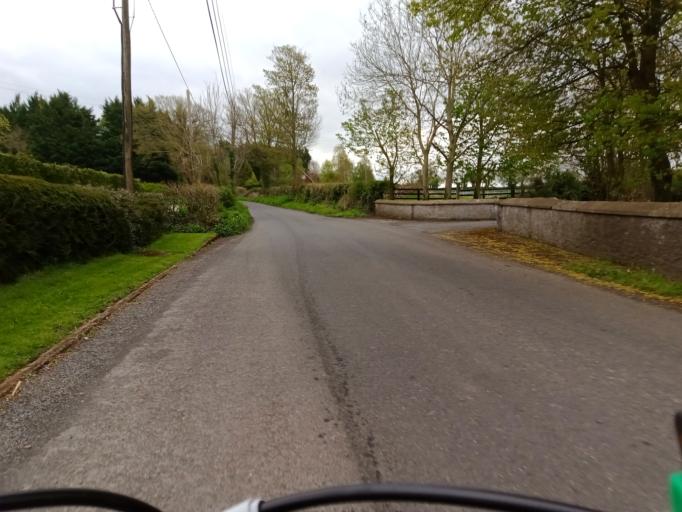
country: IE
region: Leinster
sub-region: Kilkenny
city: Kilkenny
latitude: 52.6202
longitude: -7.2753
